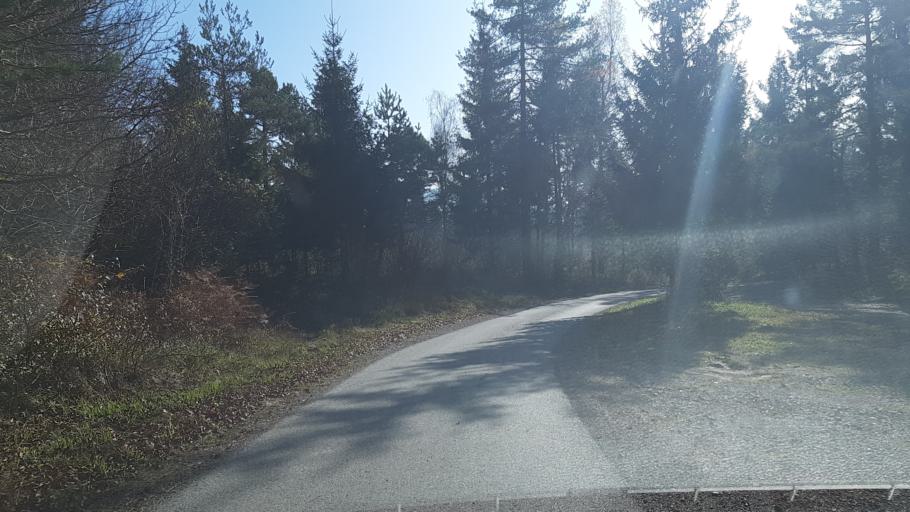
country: SI
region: Borovnica
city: Borovnica
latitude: 45.8962
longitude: 14.3541
